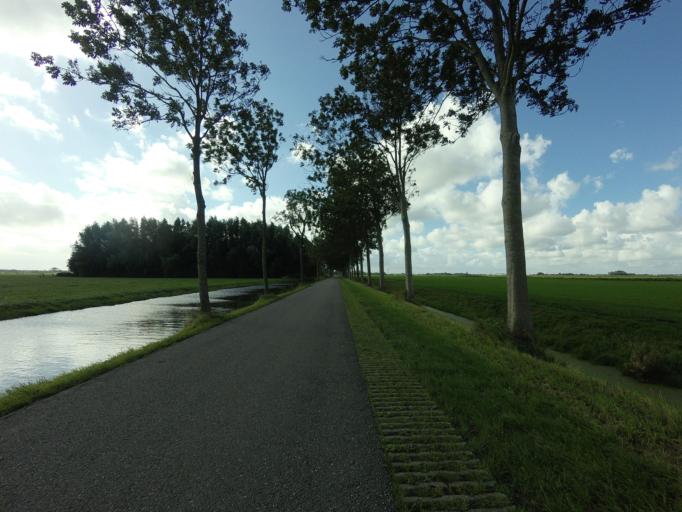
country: NL
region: North Holland
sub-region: Gemeente Hoorn
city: Hoorn
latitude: 52.6683
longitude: 5.0033
